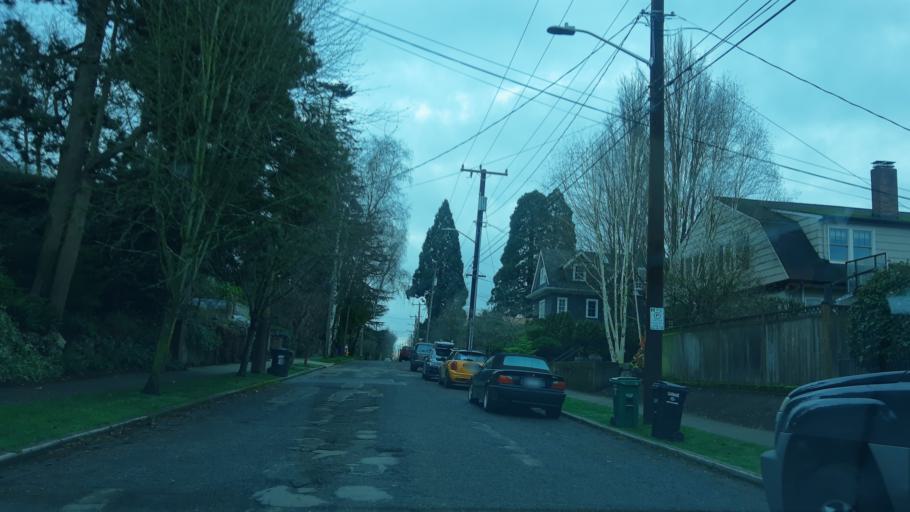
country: US
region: Washington
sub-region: King County
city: Seattle
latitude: 47.6349
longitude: -122.3191
